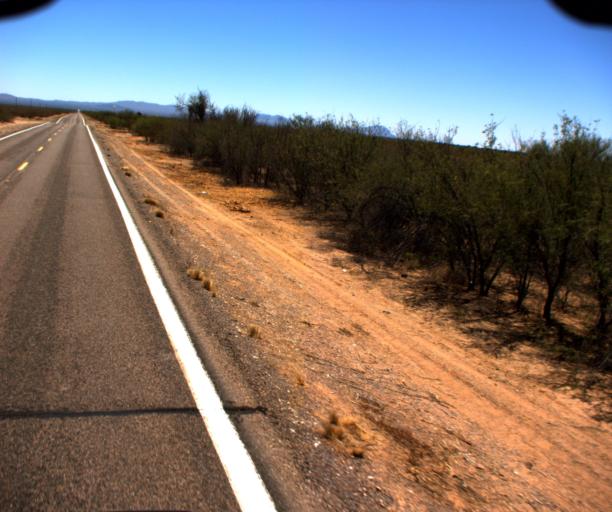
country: US
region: Arizona
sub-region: Pima County
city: Ajo
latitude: 32.1977
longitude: -112.4736
